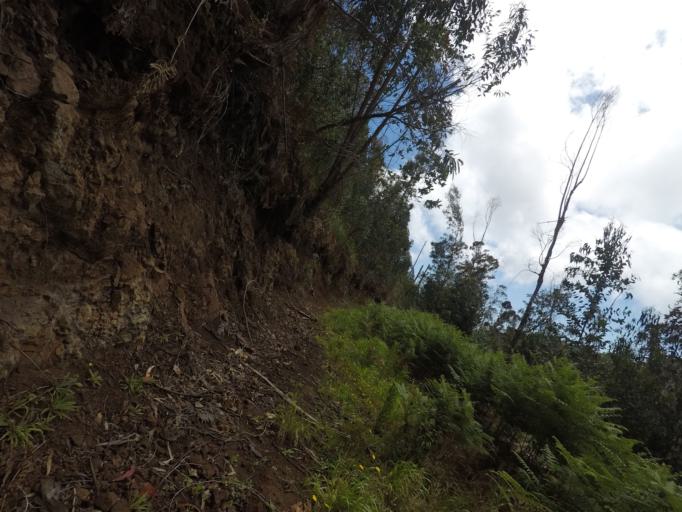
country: PT
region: Madeira
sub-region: Calheta
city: Estreito da Calheta
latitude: 32.7505
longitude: -17.1955
